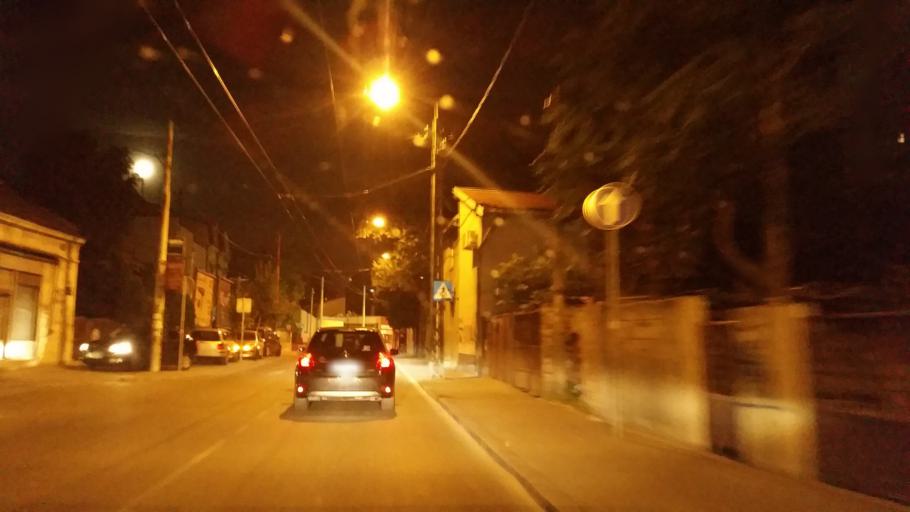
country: RS
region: Central Serbia
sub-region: Belgrade
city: Vracar
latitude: 44.7968
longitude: 20.4887
